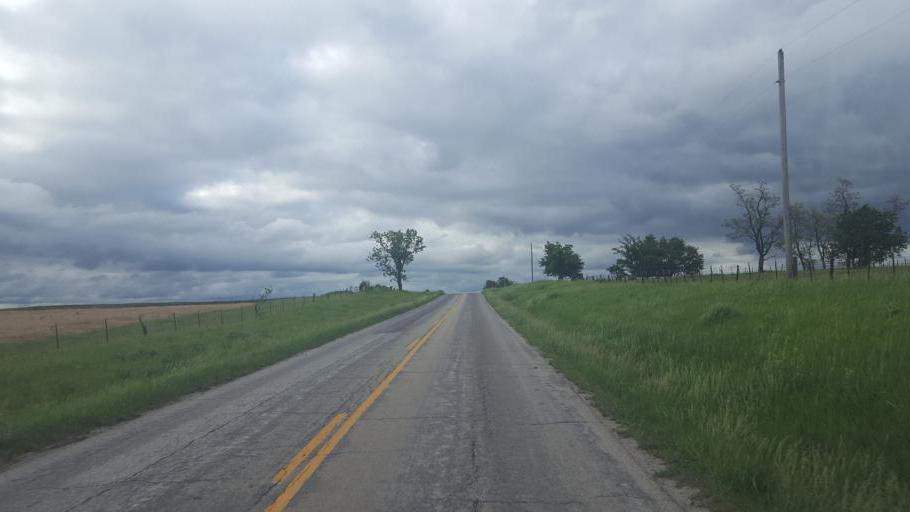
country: US
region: Missouri
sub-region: Mercer County
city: Princeton
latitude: 40.2866
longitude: -93.6803
